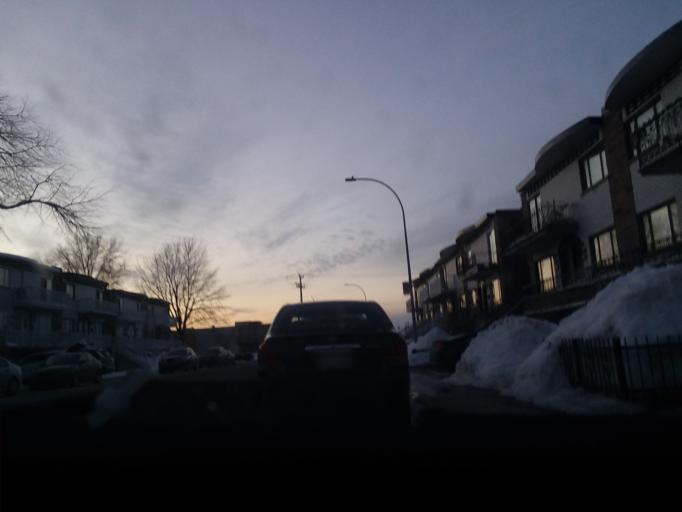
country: CA
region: Quebec
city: Montreal-Ouest
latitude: 45.4388
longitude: -73.6322
